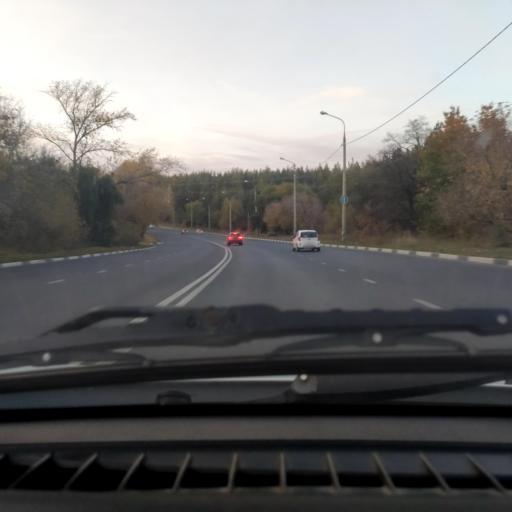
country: RU
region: Samara
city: Zhigulevsk
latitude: 53.5008
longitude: 49.4723
